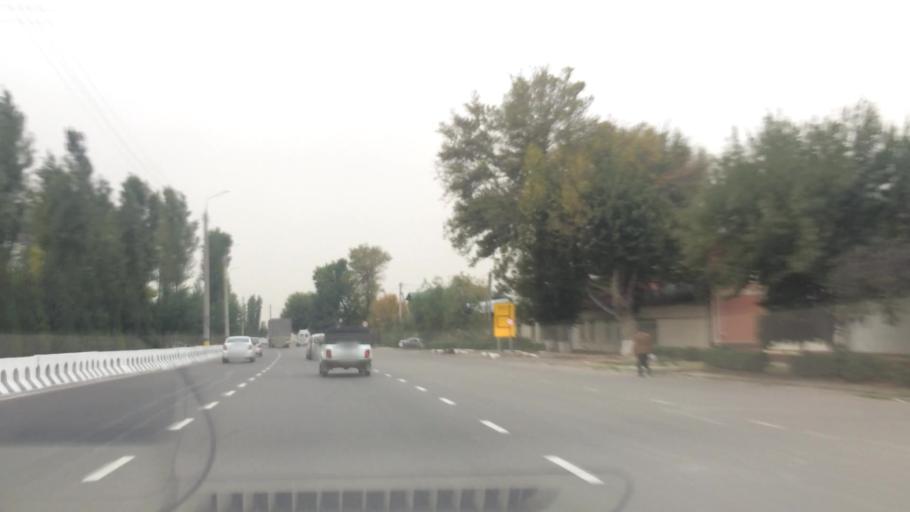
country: UZ
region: Toshkent
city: Salor
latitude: 41.3090
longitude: 69.3427
